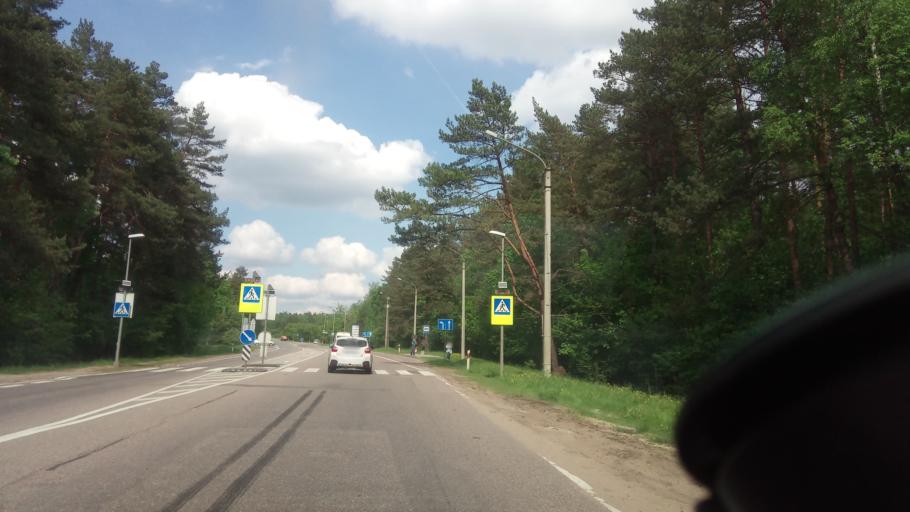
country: LT
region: Vilnius County
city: Lazdynai
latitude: 54.6373
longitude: 25.1769
